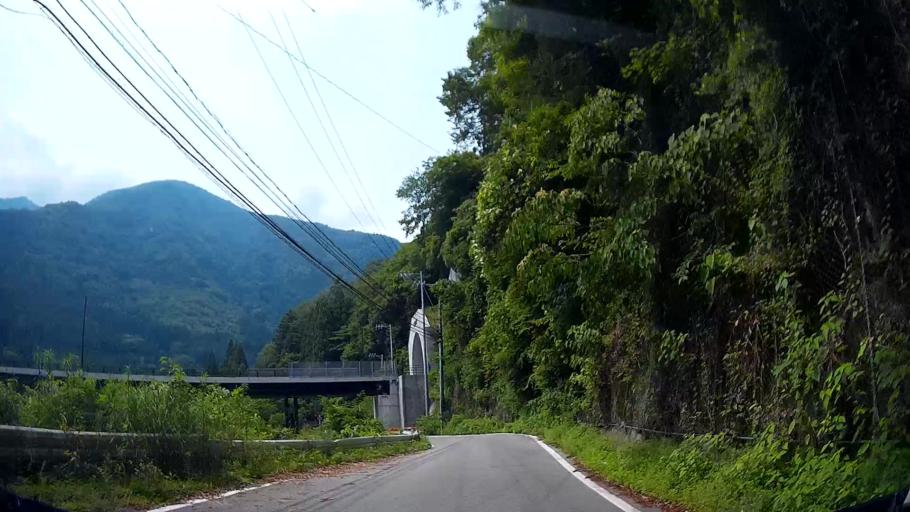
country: JP
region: Nagano
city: Iida
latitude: 35.3368
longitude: 137.9519
